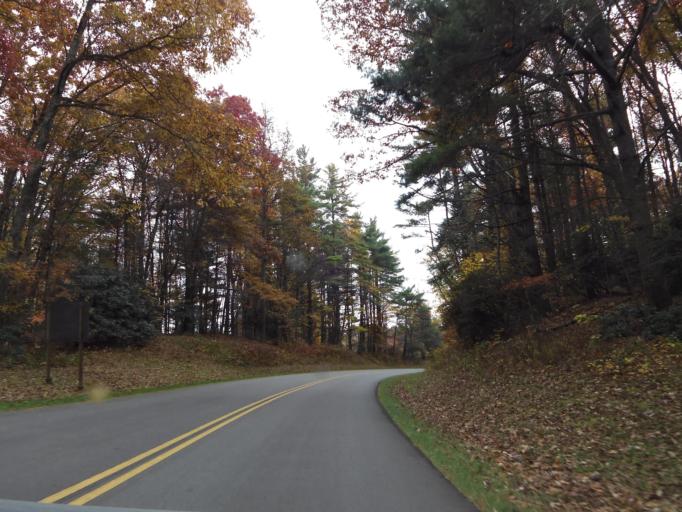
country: US
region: North Carolina
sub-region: Ashe County
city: Jefferson
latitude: 36.3409
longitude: -81.3732
